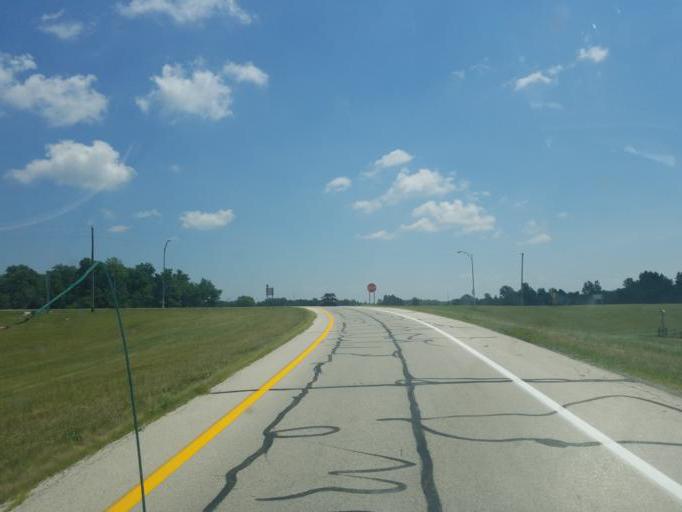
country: US
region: Ohio
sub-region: Auglaize County
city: Saint Marys
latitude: 40.5562
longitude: -84.4454
